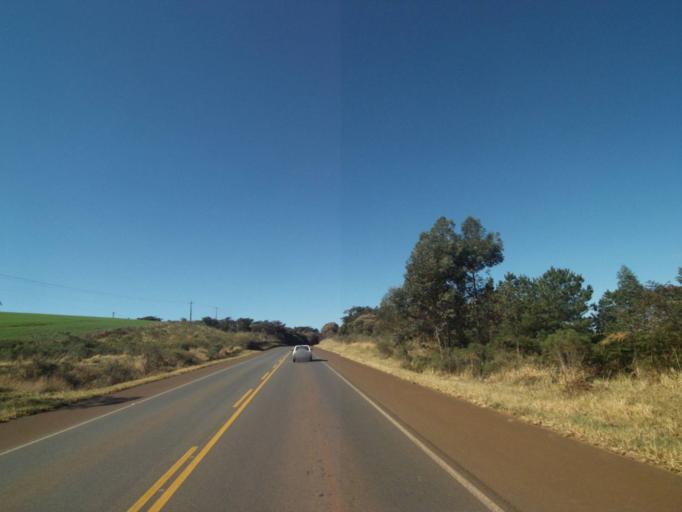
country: BR
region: Parana
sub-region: Tibagi
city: Tibagi
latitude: -24.4226
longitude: -50.3868
